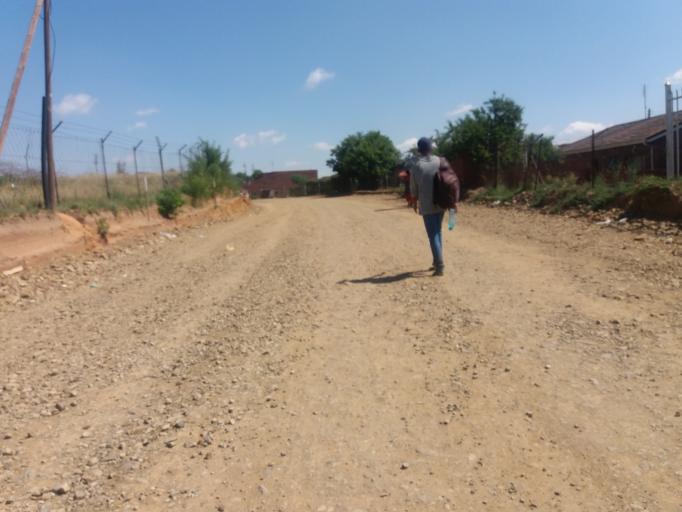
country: LS
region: Maseru
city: Maseru
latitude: -29.3164
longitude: 27.5039
